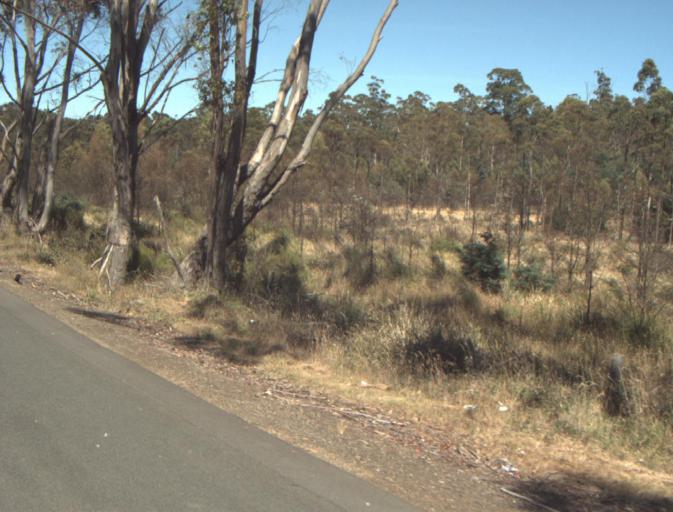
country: AU
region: Tasmania
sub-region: Launceston
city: Newstead
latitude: -41.3852
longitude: 147.2969
